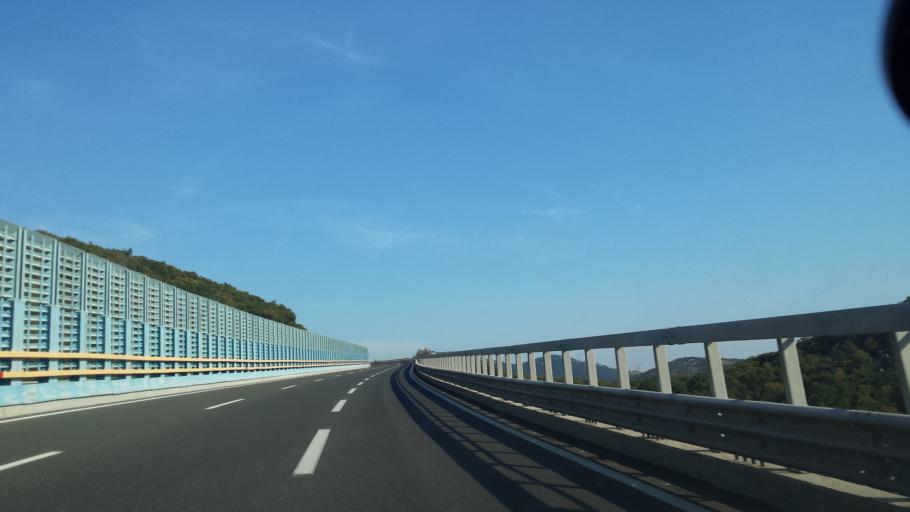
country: HR
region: Primorsko-Goranska
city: Skrljevo
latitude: 45.3661
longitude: 14.5489
